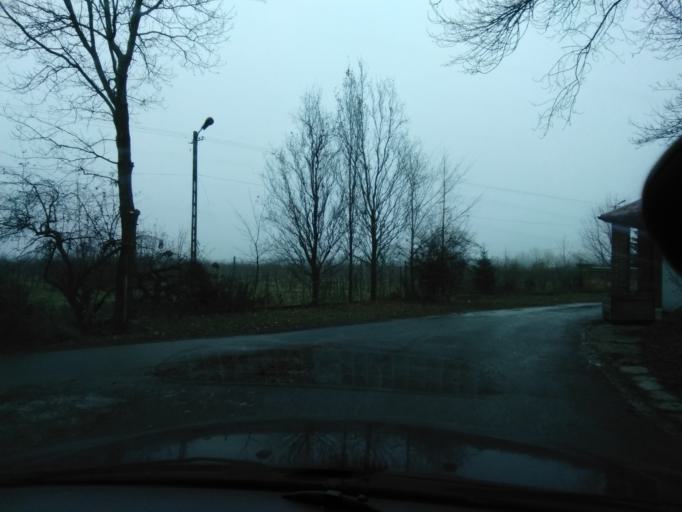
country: PL
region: Subcarpathian Voivodeship
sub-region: Powiat lancucki
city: Albigowa
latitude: 50.0300
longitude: 22.2237
